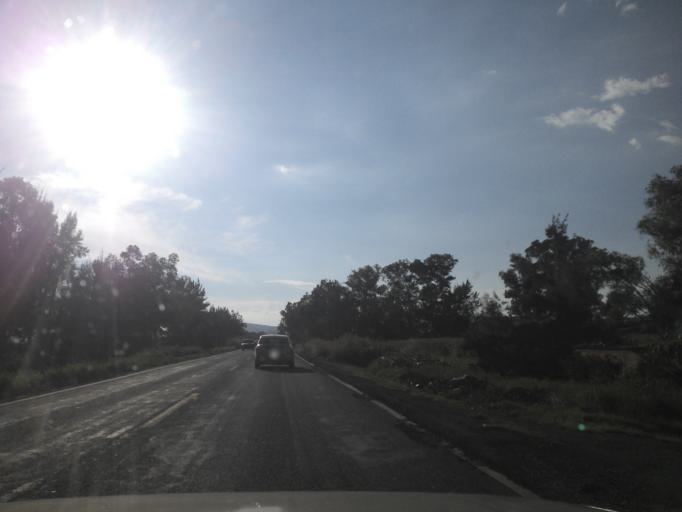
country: MX
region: Jalisco
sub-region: Tototlan
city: Nuevo Refugio de Afuera (Nuevo Refugio)
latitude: 20.5587
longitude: -102.7252
